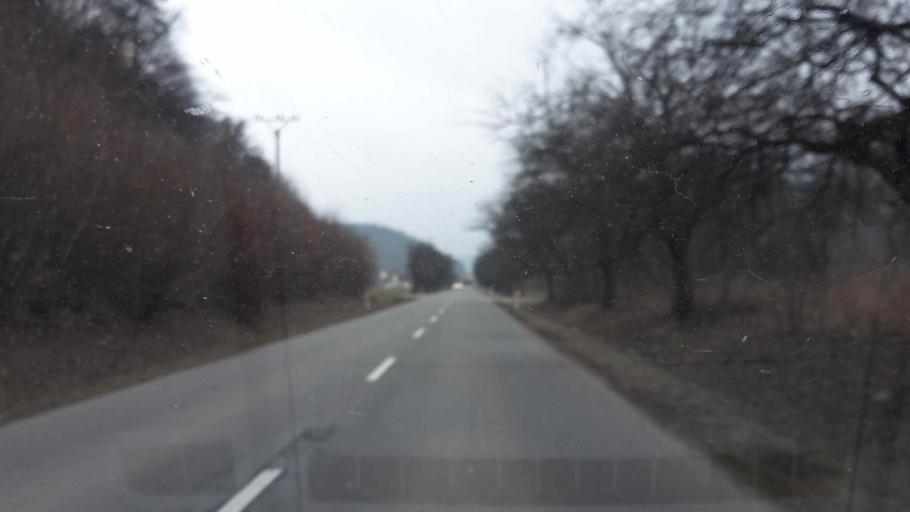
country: CZ
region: South Moravian
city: Predklasteri
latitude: 49.3658
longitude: 16.3938
